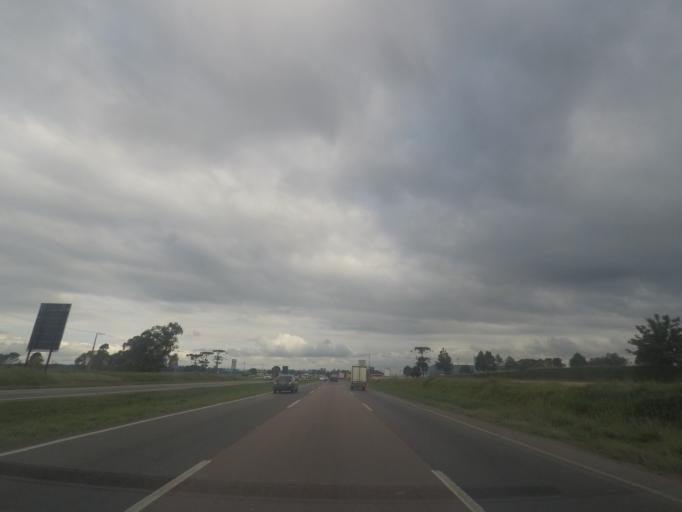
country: BR
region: Parana
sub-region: Sao Jose Dos Pinhais
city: Sao Jose dos Pinhais
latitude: -25.5467
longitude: -49.1506
